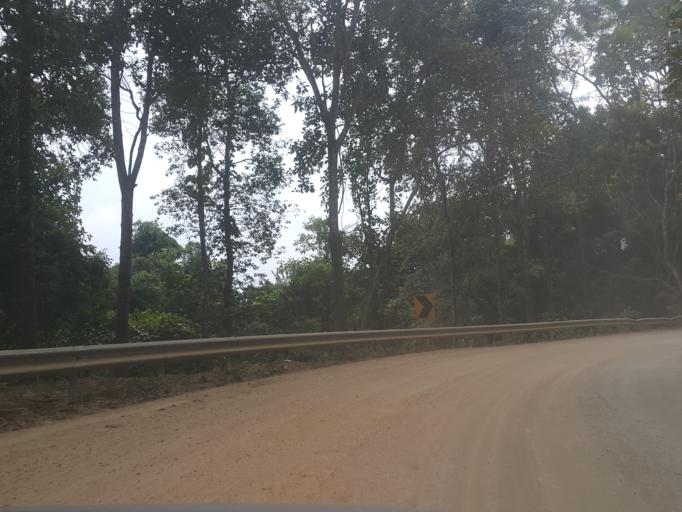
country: TH
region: Mae Hong Son
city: Mae Hi
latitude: 19.2366
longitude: 98.6611
